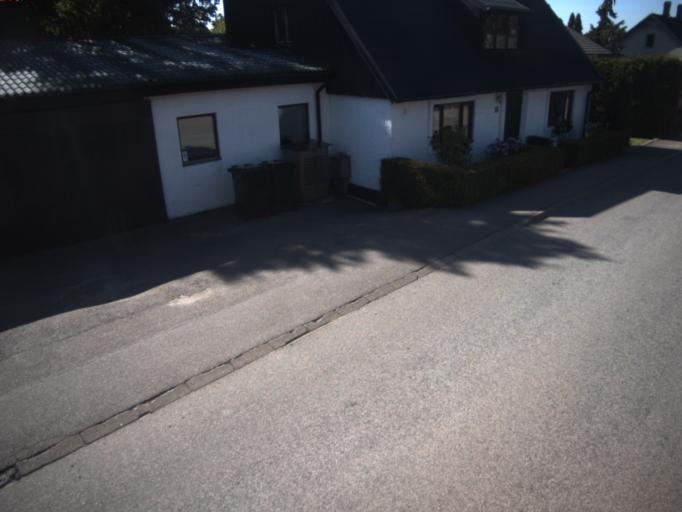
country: SE
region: Skane
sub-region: Helsingborg
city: Gantofta
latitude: 55.9884
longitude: 12.8046
